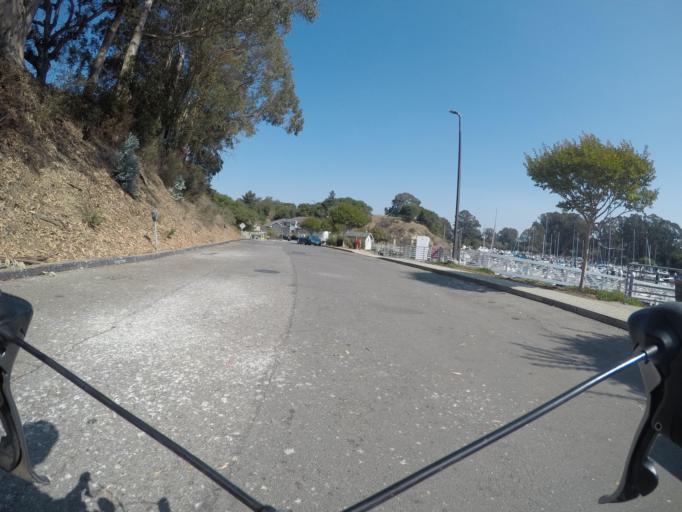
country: US
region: California
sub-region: Santa Cruz County
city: Twin Lakes
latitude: 36.9721
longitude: -122.0006
